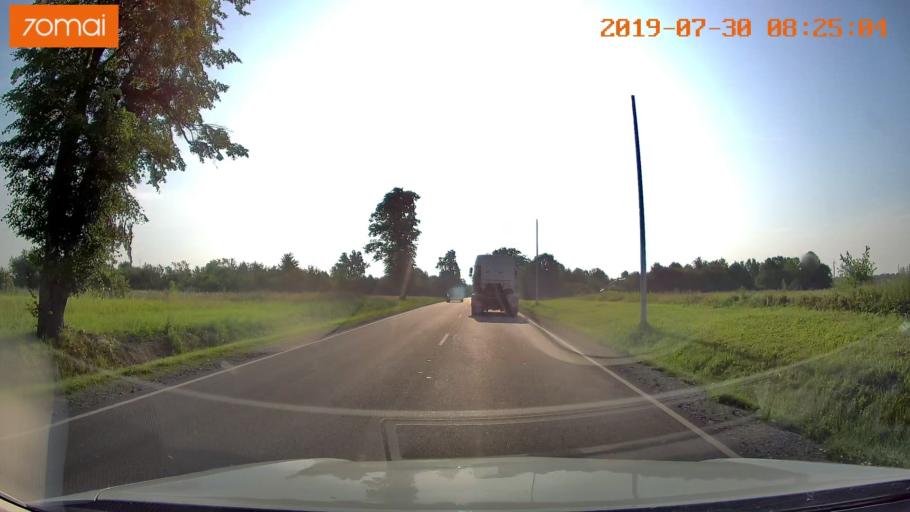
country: RU
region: Kaliningrad
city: Chernyakhovsk
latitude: 54.6238
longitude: 21.5721
